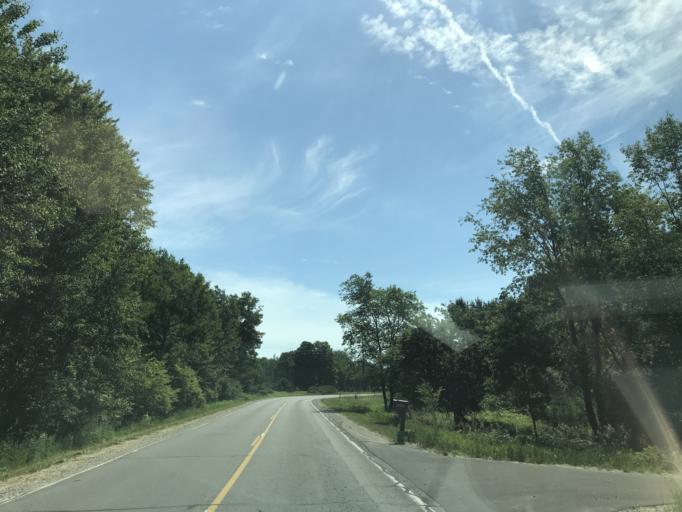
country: US
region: Michigan
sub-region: Grand Traverse County
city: Traverse City
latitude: 44.6582
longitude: -85.7199
